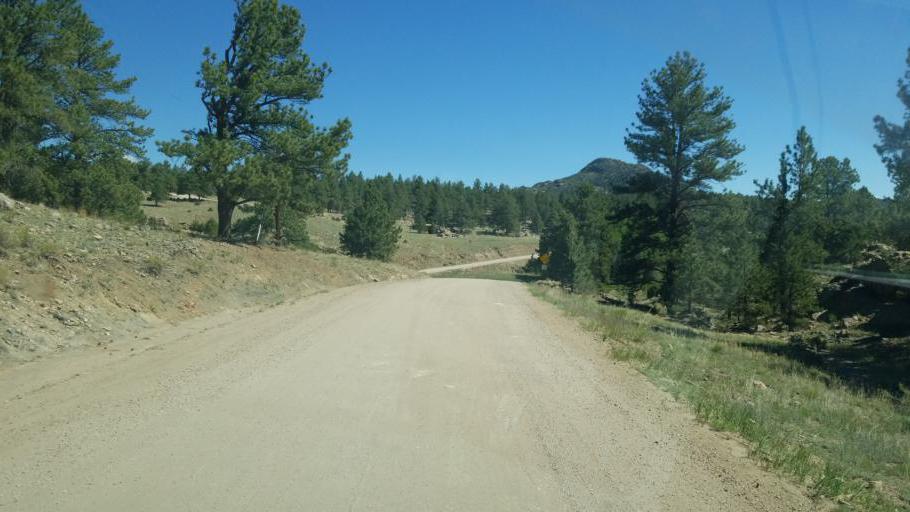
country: US
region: Colorado
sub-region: Custer County
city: Westcliffe
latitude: 38.2099
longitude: -105.4436
